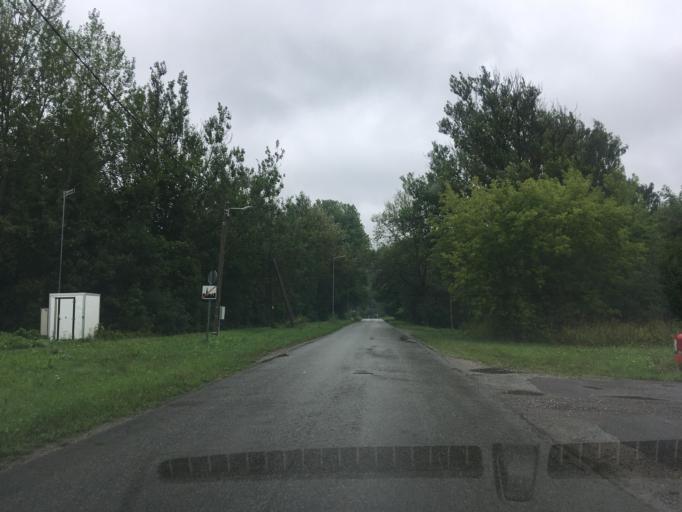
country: EE
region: Ida-Virumaa
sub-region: Kivioli linn
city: Kivioli
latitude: 59.3581
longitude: 26.9593
